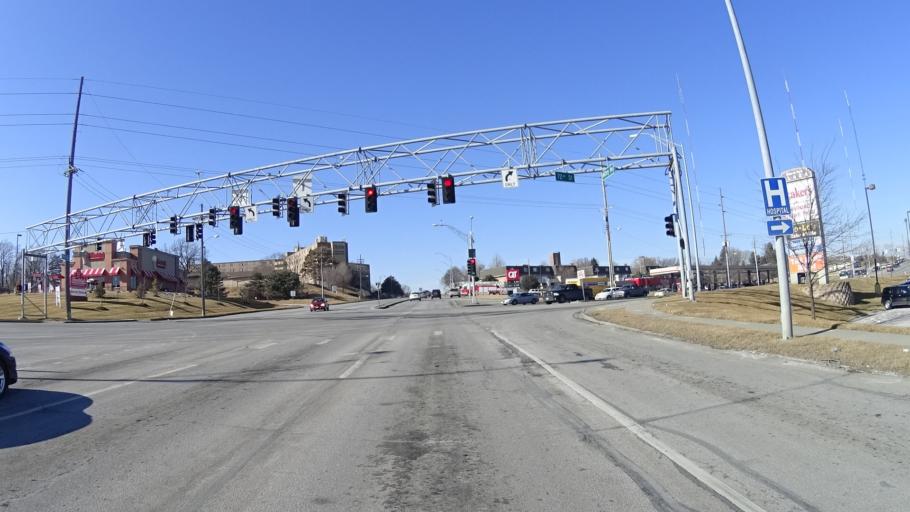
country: US
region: Nebraska
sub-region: Douglas County
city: Omaha
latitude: 41.2975
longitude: -96.0234
